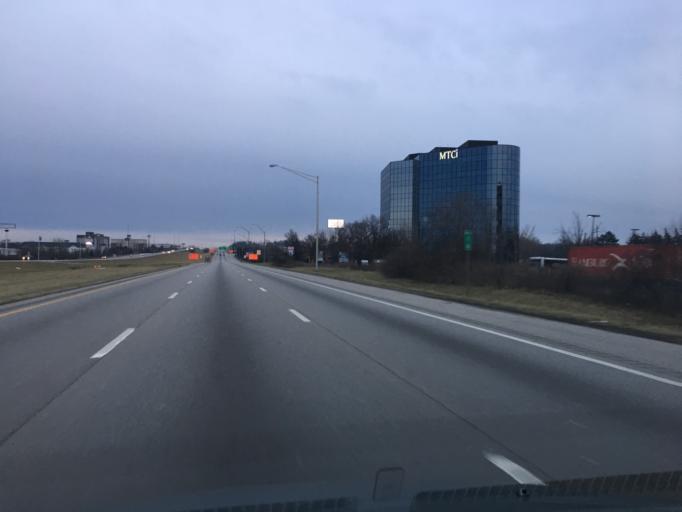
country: US
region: Ohio
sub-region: Hamilton County
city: Glendale
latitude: 39.2792
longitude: -84.4414
